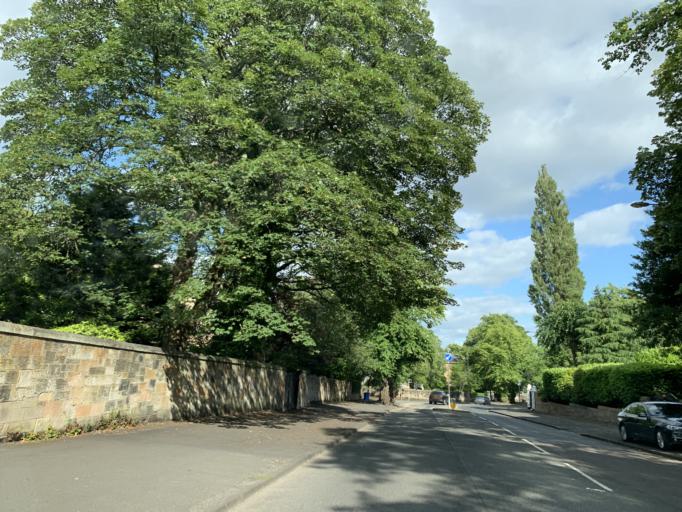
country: GB
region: Scotland
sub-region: East Renfrewshire
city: Giffnock
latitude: 55.8433
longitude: -4.2931
